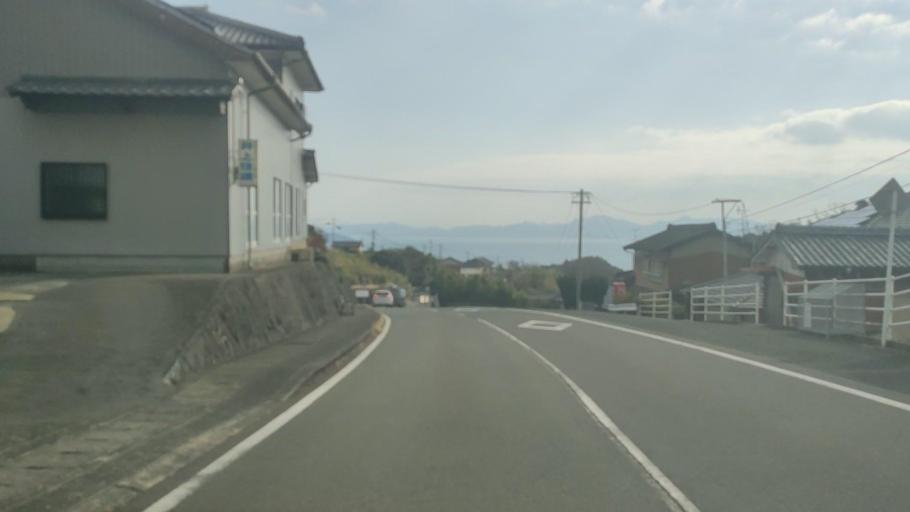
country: JP
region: Nagasaki
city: Shimabara
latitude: 32.6765
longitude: 130.2807
